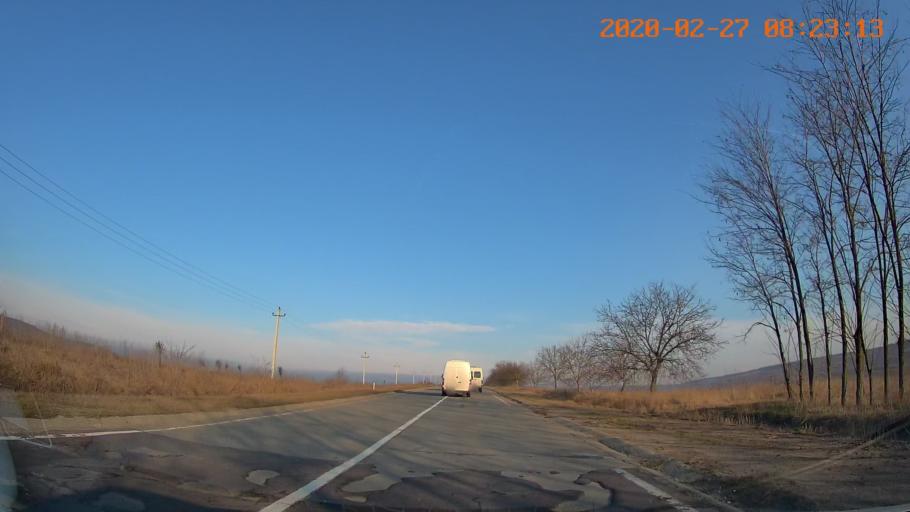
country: MD
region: Straseni
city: Straseni
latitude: 47.2590
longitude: 28.5970
